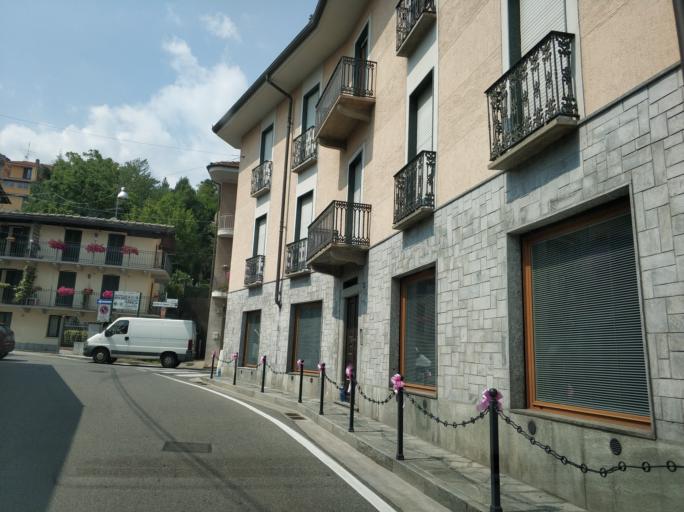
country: IT
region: Piedmont
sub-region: Provincia di Torino
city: Lanzo Torinese
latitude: 45.2748
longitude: 7.4738
